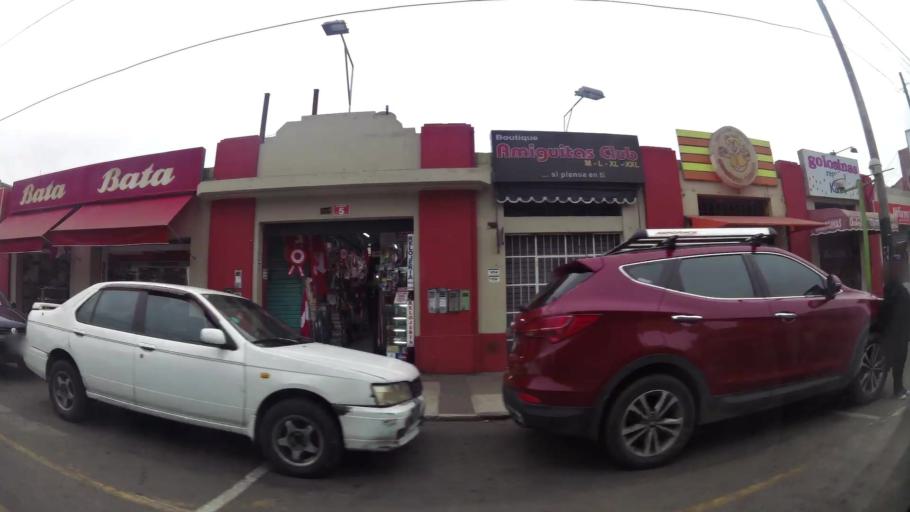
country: PE
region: Lima
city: Lima
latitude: -12.0738
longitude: -77.0497
